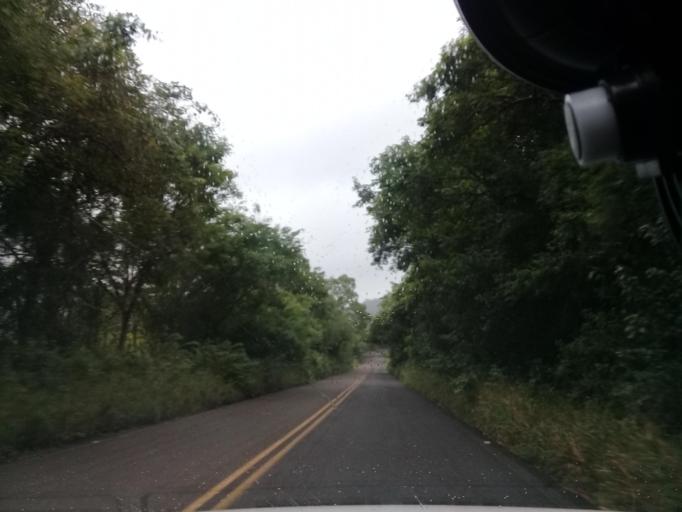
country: MX
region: Veracruz
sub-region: Chalma
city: San Pedro Coyutla
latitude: 21.2185
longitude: -98.3835
